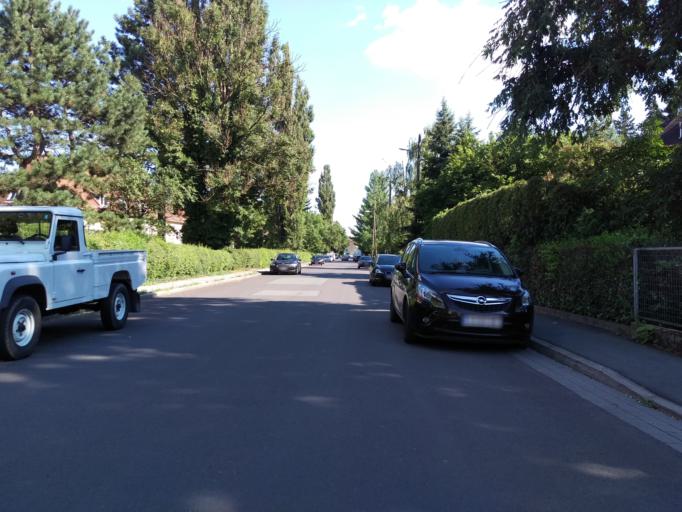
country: AT
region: Styria
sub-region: Graz Stadt
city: Wetzelsdorf
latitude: 47.0615
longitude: 15.3892
